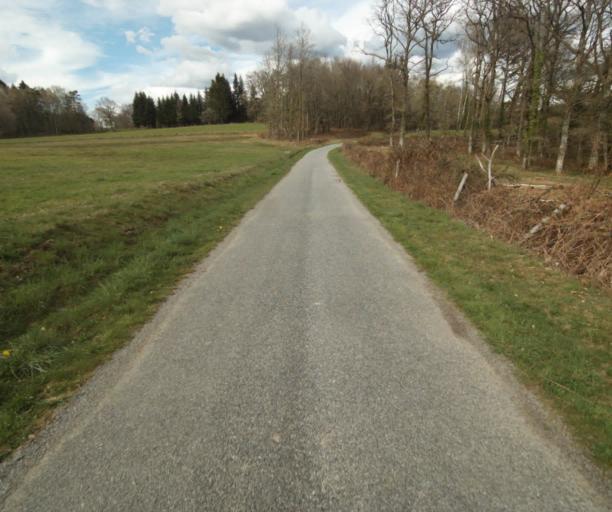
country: FR
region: Limousin
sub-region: Departement de la Correze
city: Argentat
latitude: 45.1962
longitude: 1.9270
